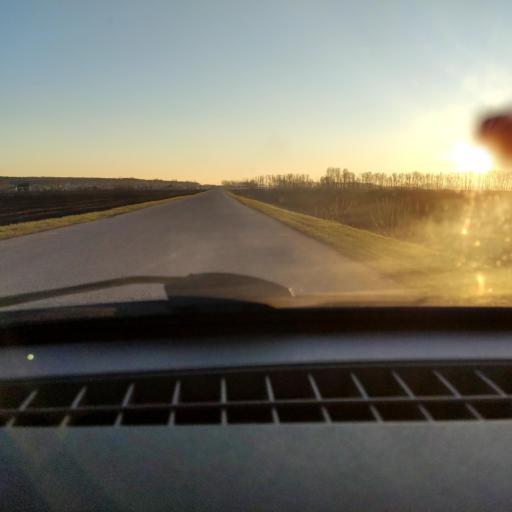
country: RU
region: Bashkortostan
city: Avdon
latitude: 54.5443
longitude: 55.6502
